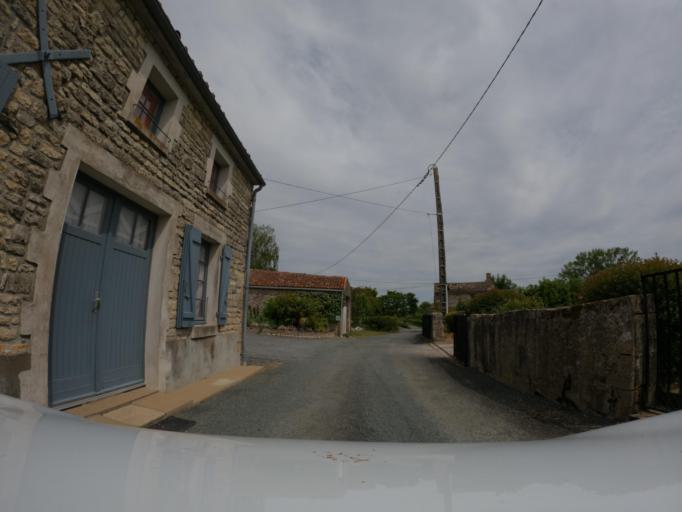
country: FR
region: Pays de la Loire
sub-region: Departement de la Vendee
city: Saint-Hilaire-des-Loges
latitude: 46.4909
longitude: -0.6339
